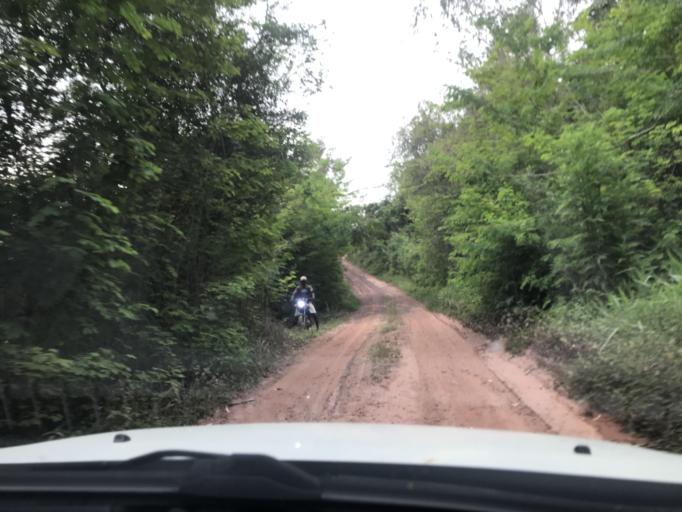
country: BR
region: Bahia
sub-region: Entre Rios
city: Entre Rios
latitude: -12.0951
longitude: -38.1960
